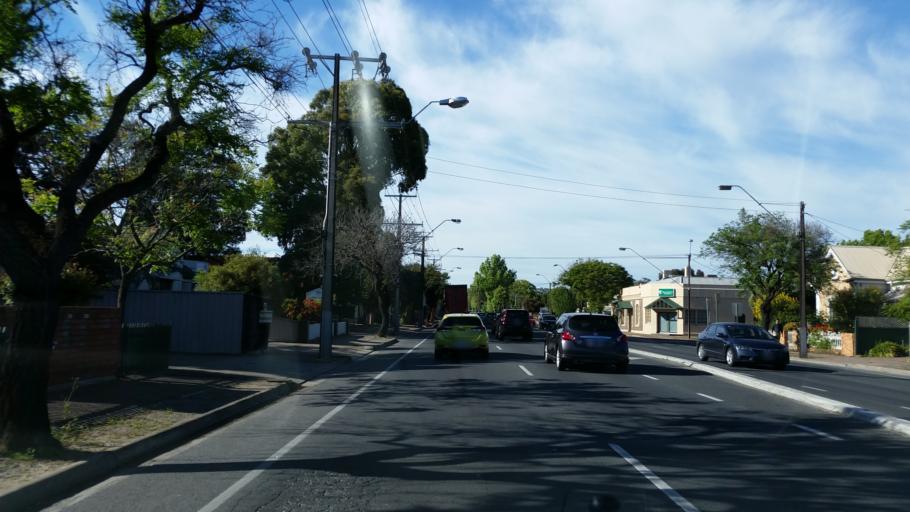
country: AU
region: South Australia
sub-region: Norwood Payneham St Peters
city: Payneham
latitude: -34.9005
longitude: 138.6395
